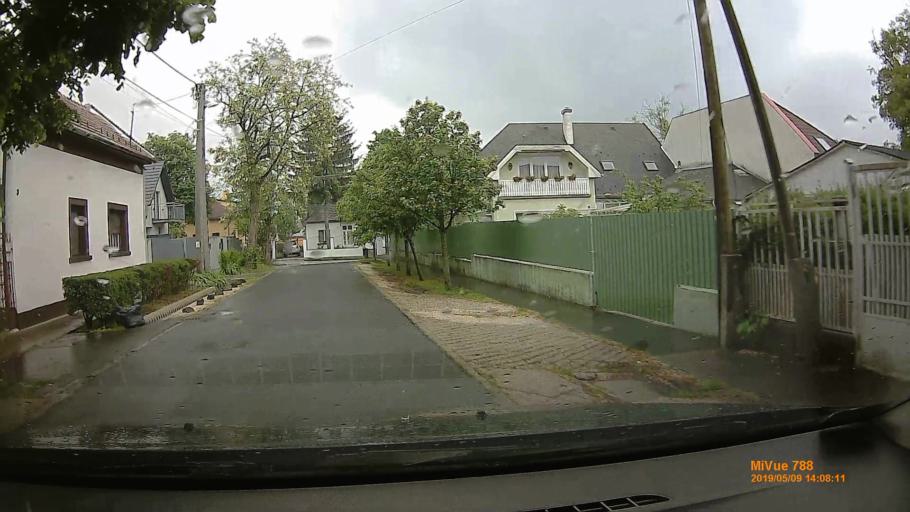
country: HU
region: Budapest
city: Budapest XVI. keruelet
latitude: 47.5108
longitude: 19.1725
